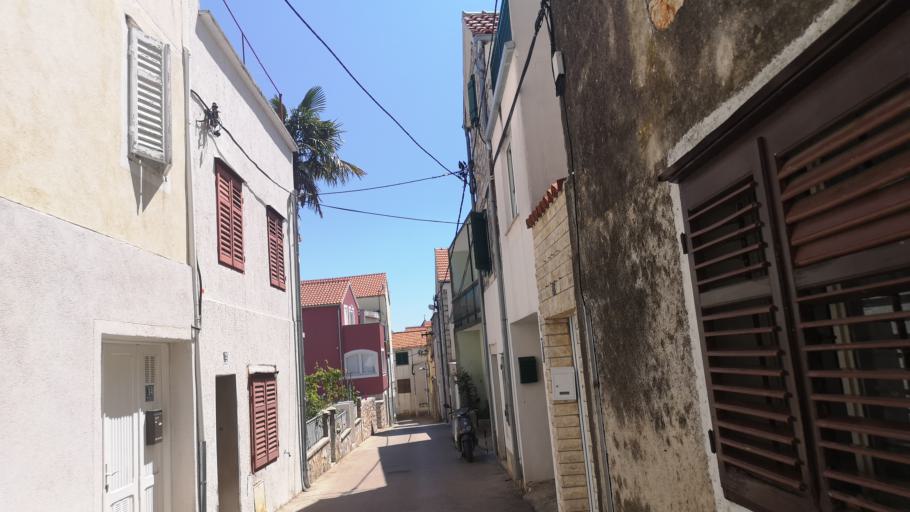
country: HR
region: Sibensko-Kniniska
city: Vodice
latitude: 43.7580
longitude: 15.7722
